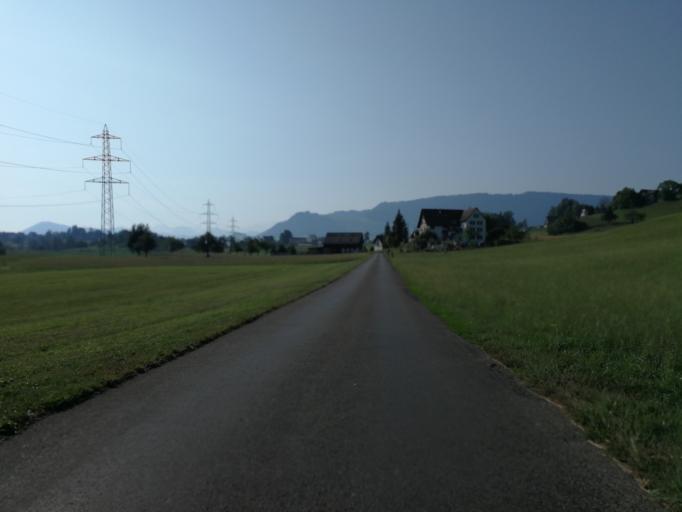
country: CH
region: Zurich
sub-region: Bezirk Horgen
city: Waedenswil / Untermosen-Fuhr
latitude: 47.2050
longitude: 8.6453
